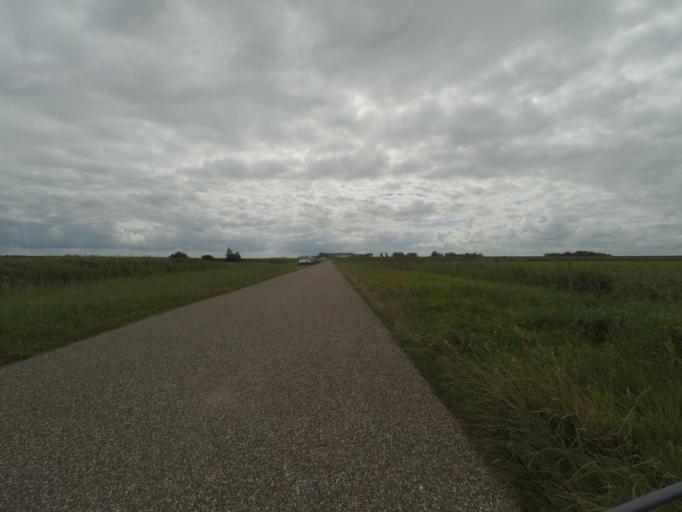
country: NL
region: Friesland
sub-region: Gemeente Dongeradeel
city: Anjum
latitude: 53.3450
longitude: 6.1529
